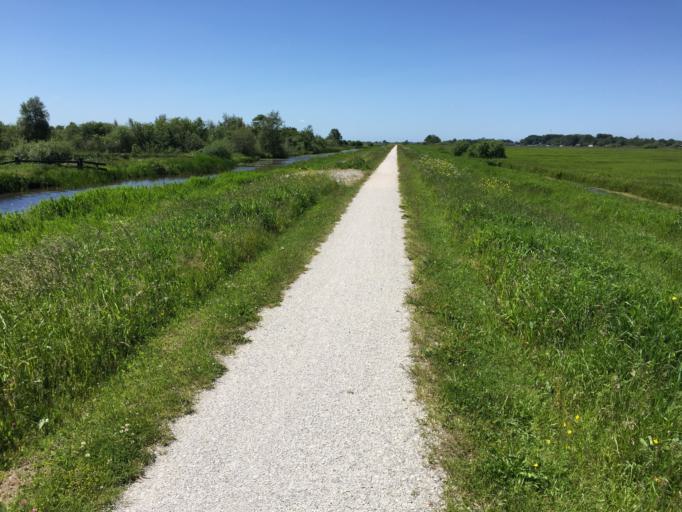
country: NL
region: Friesland
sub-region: Gemeente Smallingerland
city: Oudega
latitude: 53.1027
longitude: 5.9713
